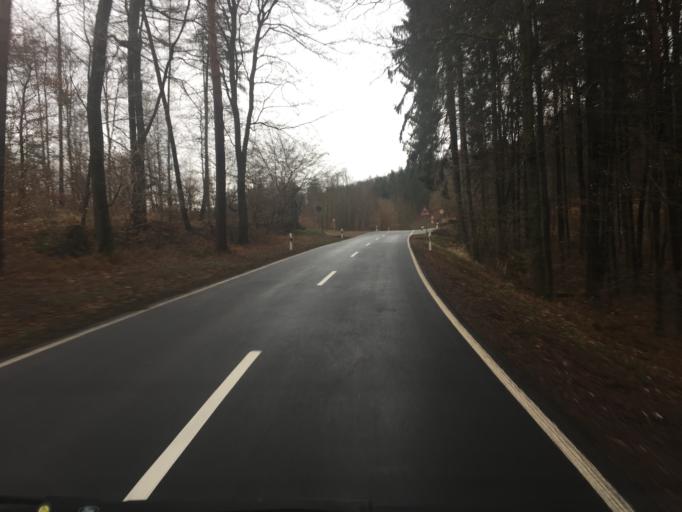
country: DE
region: Bavaria
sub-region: Regierungsbezirk Unterfranken
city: Johannesberg
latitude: 50.0463
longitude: 9.1046
